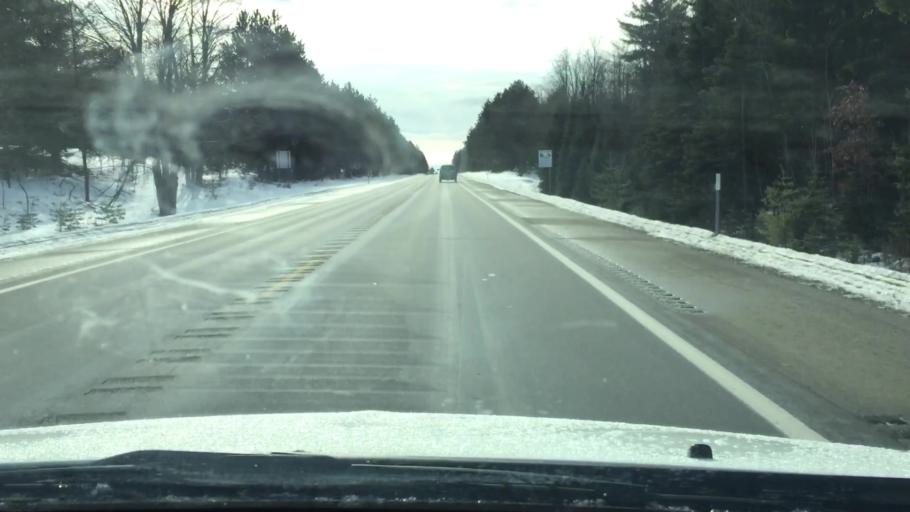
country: US
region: Michigan
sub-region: Kalkaska County
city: Kalkaska
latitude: 44.6971
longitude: -85.2079
